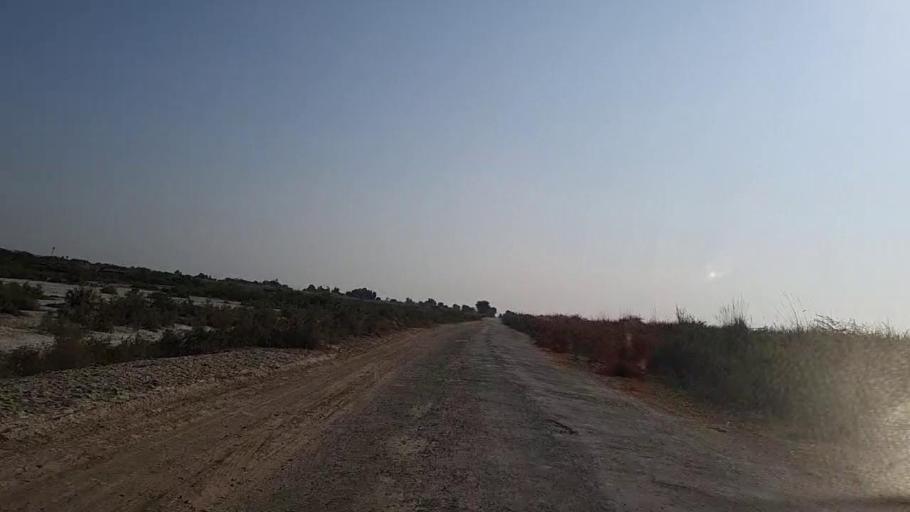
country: PK
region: Sindh
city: Tando Mittha Khan
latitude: 25.9040
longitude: 69.0772
